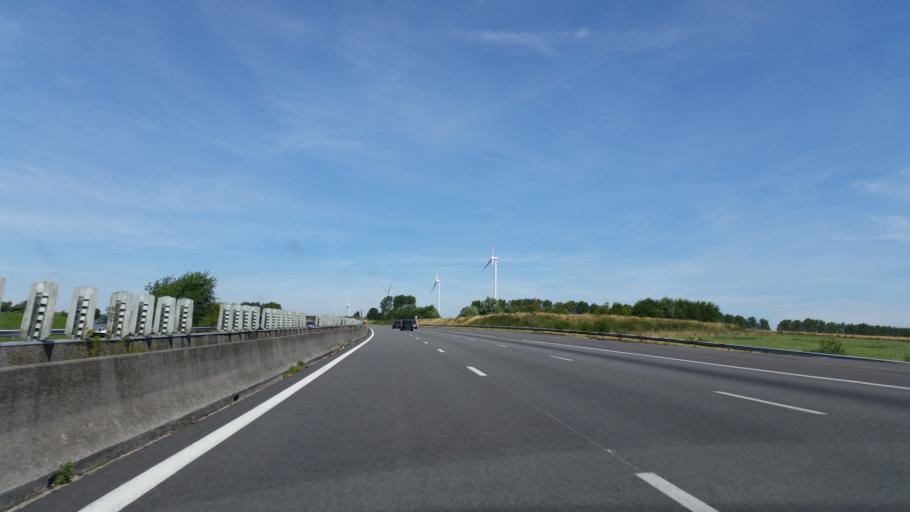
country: FR
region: Picardie
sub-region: Departement de la Somme
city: Moislains
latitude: 50.0234
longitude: 2.8842
